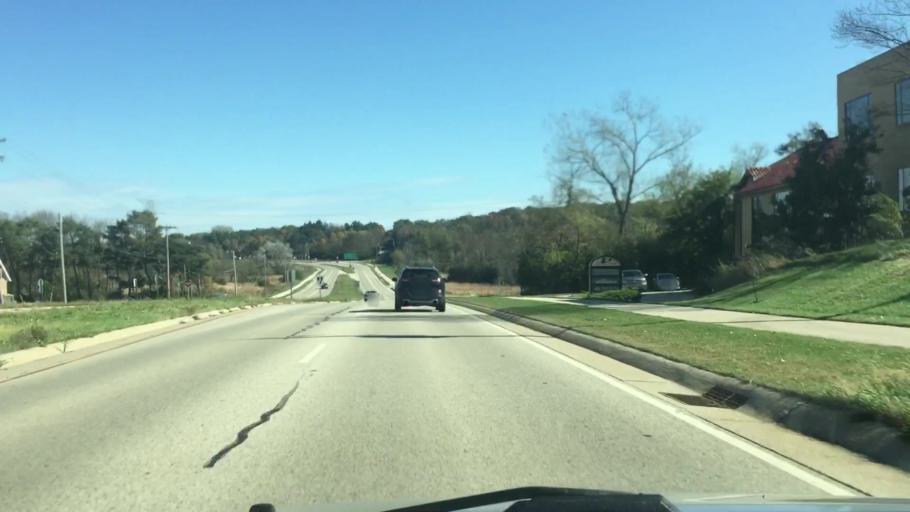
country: US
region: Wisconsin
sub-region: Waukesha County
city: Waukesha
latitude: 43.0137
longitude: -88.1799
